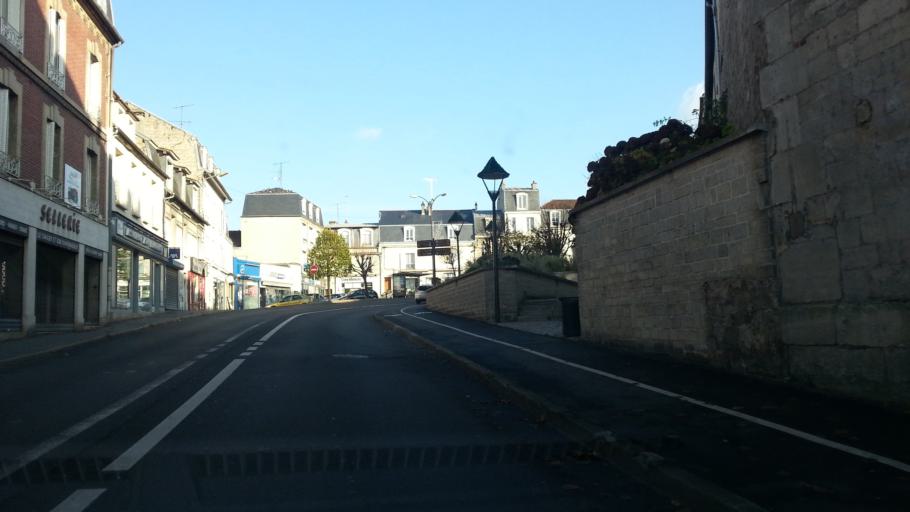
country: FR
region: Picardie
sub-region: Departement de l'Oise
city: Chantilly
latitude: 49.1946
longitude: 2.4647
